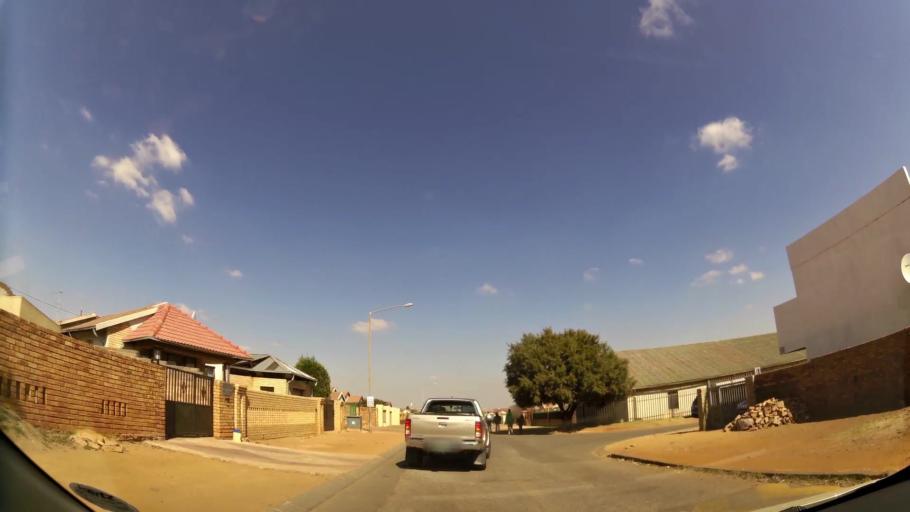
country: ZA
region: Gauteng
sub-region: West Rand District Municipality
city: Krugersdorp
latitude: -26.1503
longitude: 27.7716
